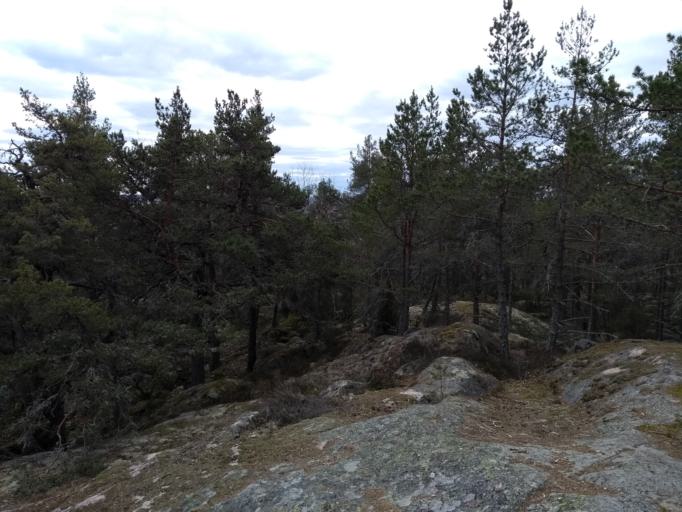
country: SE
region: OEstergoetland
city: Lindo
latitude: 58.6680
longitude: 16.2553
